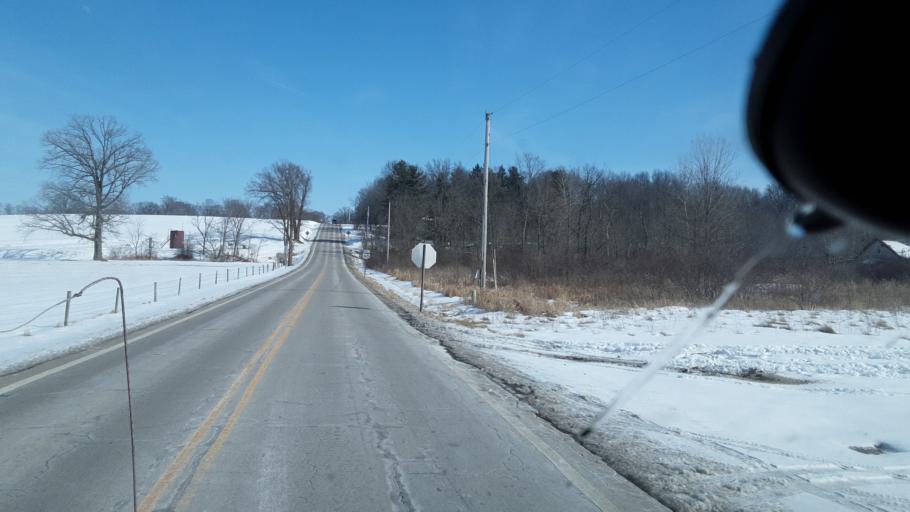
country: US
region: Ohio
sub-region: Mahoning County
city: Sebring
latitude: 40.9449
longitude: -80.9461
